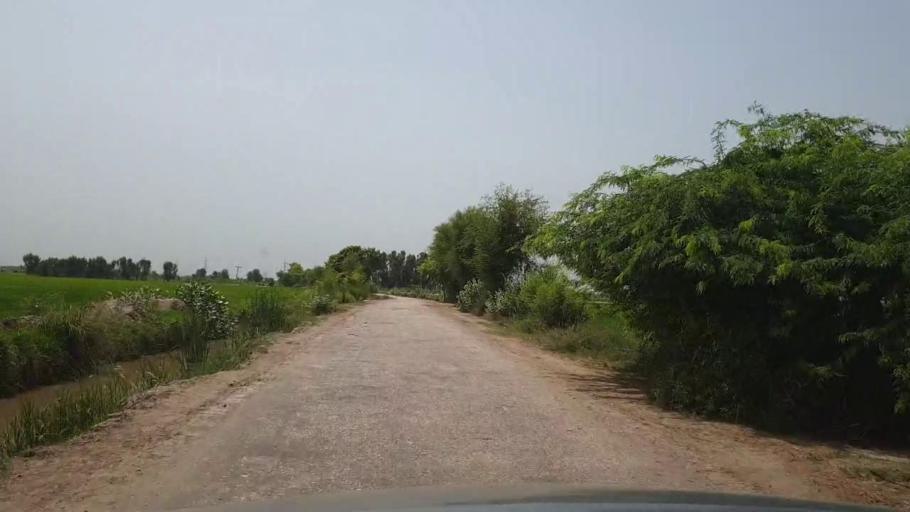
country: PK
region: Sindh
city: Madeji
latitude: 27.7748
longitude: 68.4321
